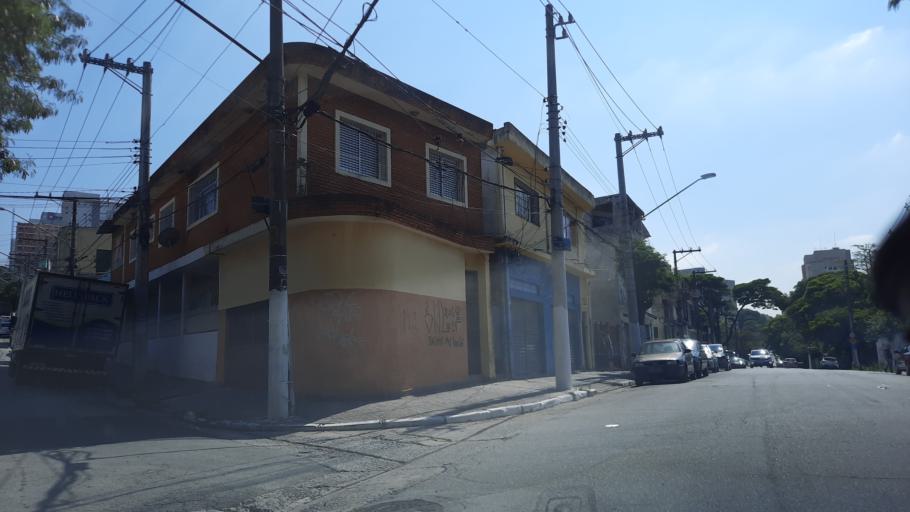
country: BR
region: Sao Paulo
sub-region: Sao Paulo
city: Sao Paulo
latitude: -23.5025
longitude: -46.6822
